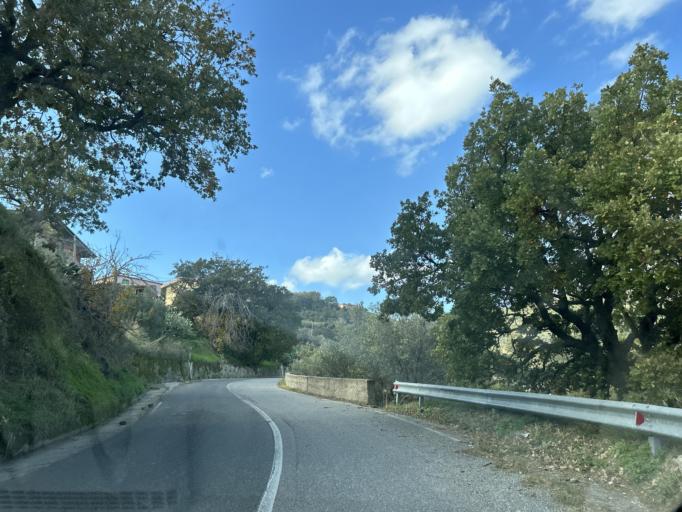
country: IT
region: Calabria
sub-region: Provincia di Catanzaro
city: Montepaone
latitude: 38.7223
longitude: 16.5065
